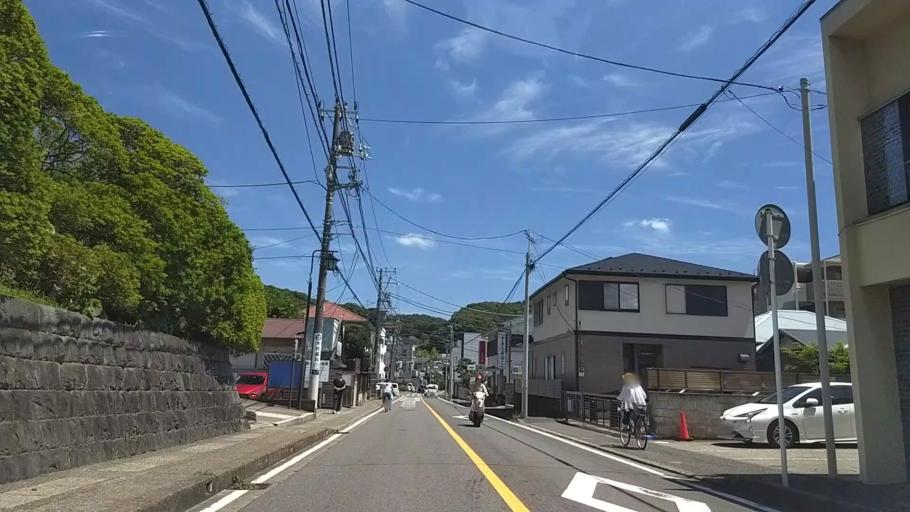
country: JP
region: Kanagawa
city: Kamakura
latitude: 35.3139
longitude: 139.5551
